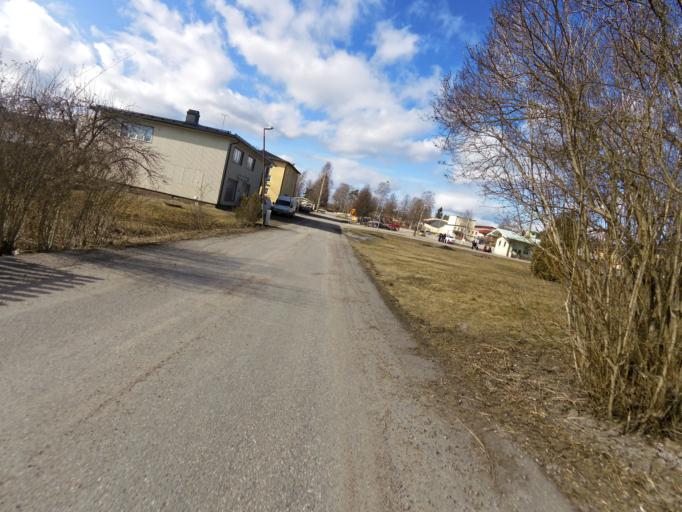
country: SE
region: Gaevleborg
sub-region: Hofors Kommun
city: Hofors
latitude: 60.5447
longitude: 16.2877
